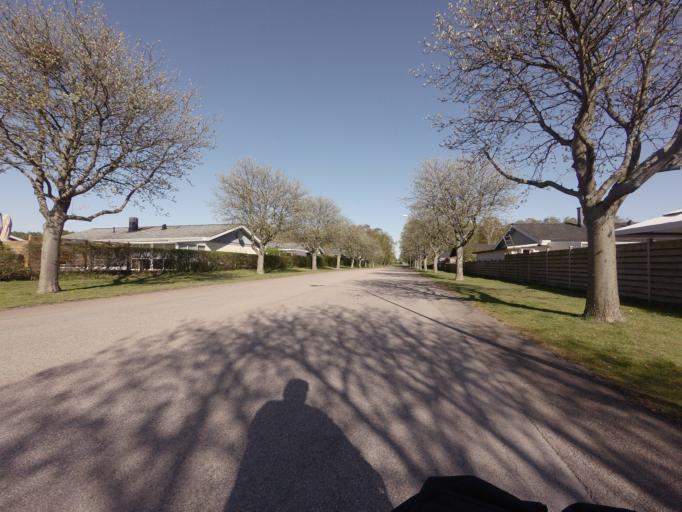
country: SE
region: Skane
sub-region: Landskrona
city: Asmundtorp
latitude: 55.8495
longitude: 12.9121
